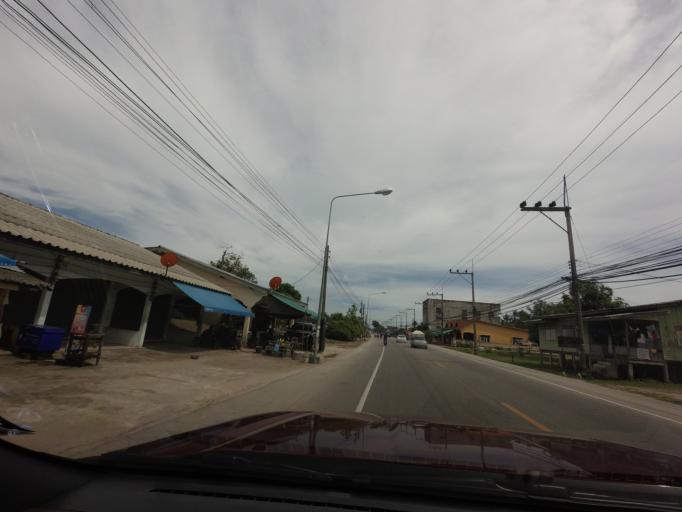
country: TH
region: Narathiwat
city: Tak Bai
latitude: 6.2505
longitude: 102.0667
